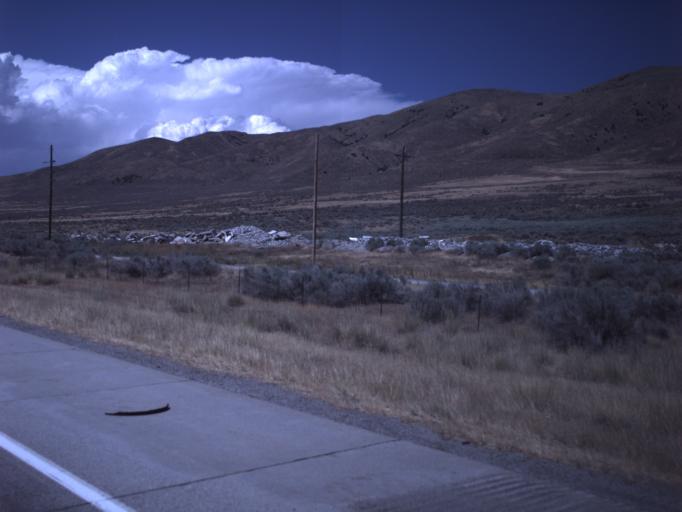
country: US
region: Utah
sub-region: Box Elder County
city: Garland
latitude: 41.7520
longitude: -112.2591
